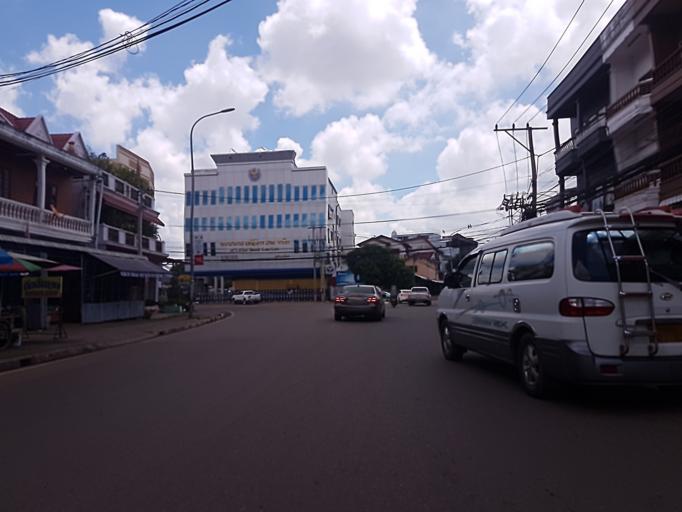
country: LA
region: Vientiane
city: Vientiane
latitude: 17.9590
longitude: 102.6236
